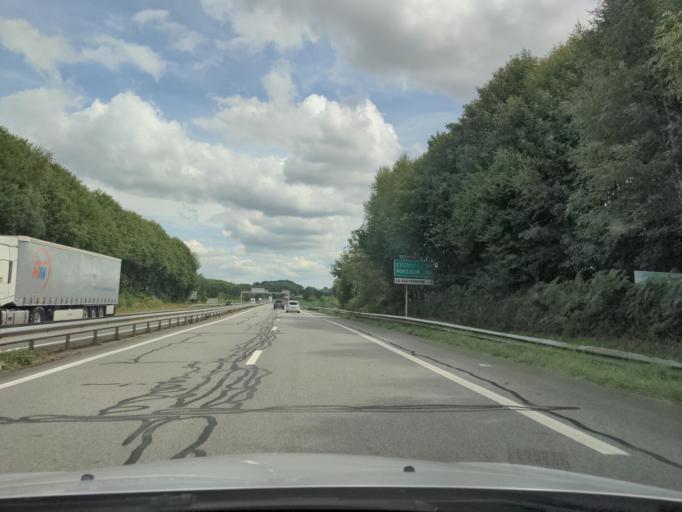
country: FR
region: Limousin
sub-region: Departement de la Creuse
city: Saint-Maurice-la-Souterraine
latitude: 46.2152
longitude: 1.4421
